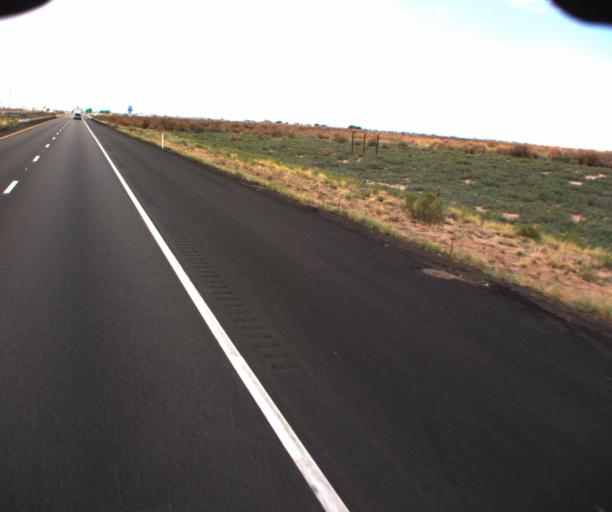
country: US
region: Arizona
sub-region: Navajo County
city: Winslow
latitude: 35.0111
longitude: -110.6492
